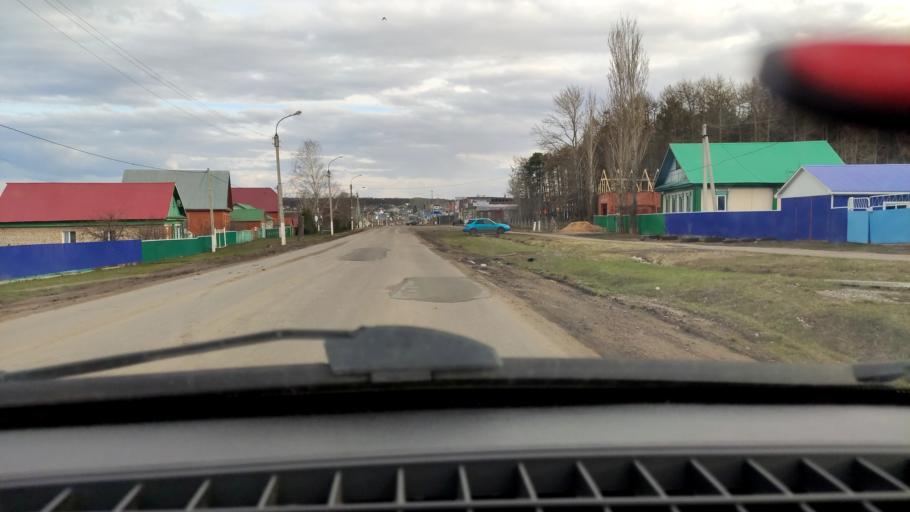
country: RU
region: Bashkortostan
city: Tolbazy
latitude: 54.0271
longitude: 55.8847
